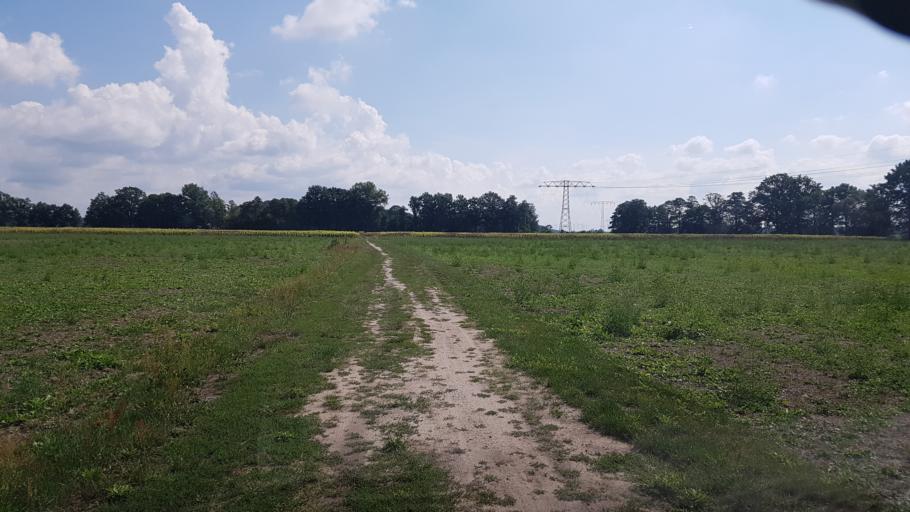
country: DE
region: Brandenburg
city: Sonnewalde
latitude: 51.6717
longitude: 13.6624
